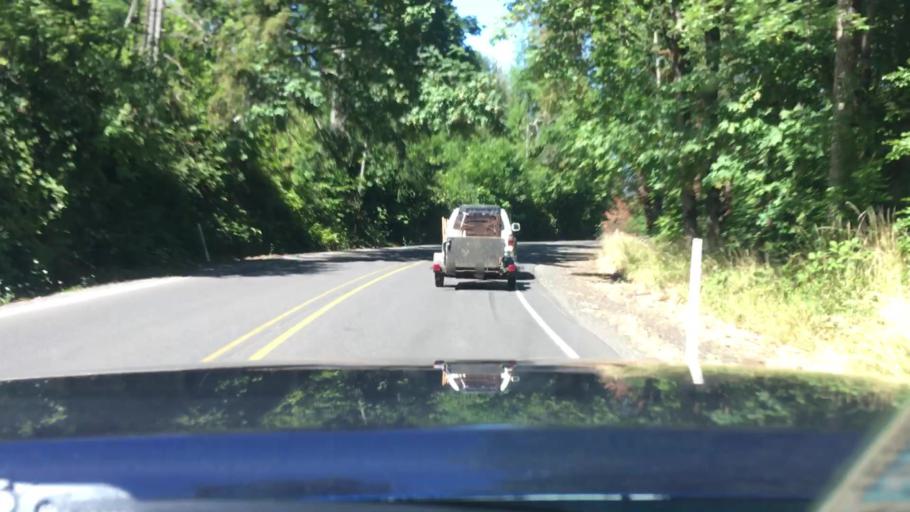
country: US
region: Oregon
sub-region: Lane County
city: Cottage Grove
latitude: 43.8249
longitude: -123.0454
